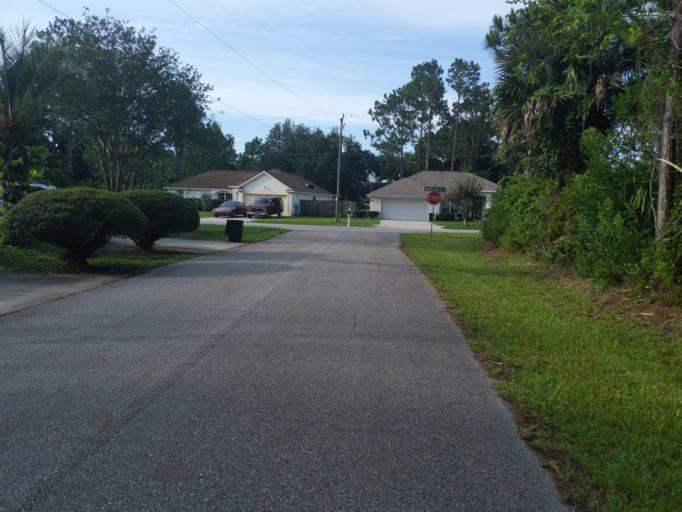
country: US
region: Florida
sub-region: Flagler County
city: Bunnell
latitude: 29.5216
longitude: -81.2375
